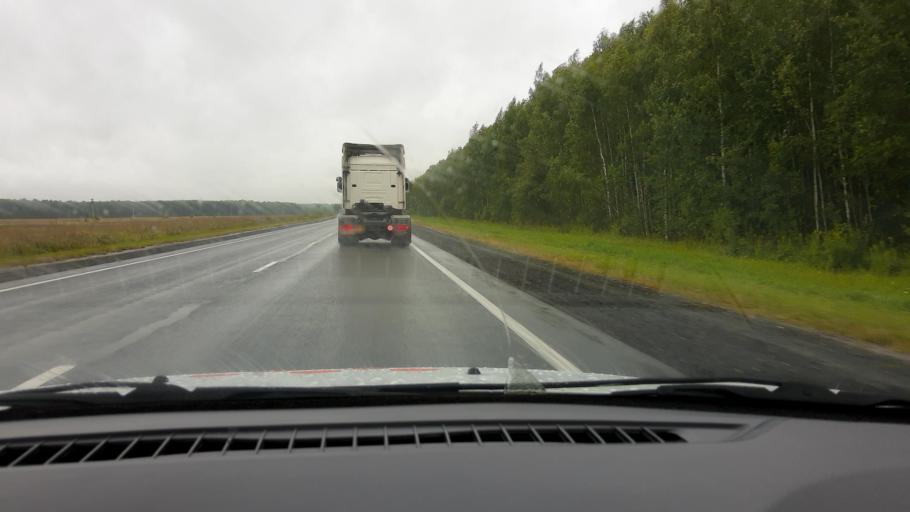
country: RU
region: Nizjnij Novgorod
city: Spasskoye
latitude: 56.0430
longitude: 45.6233
